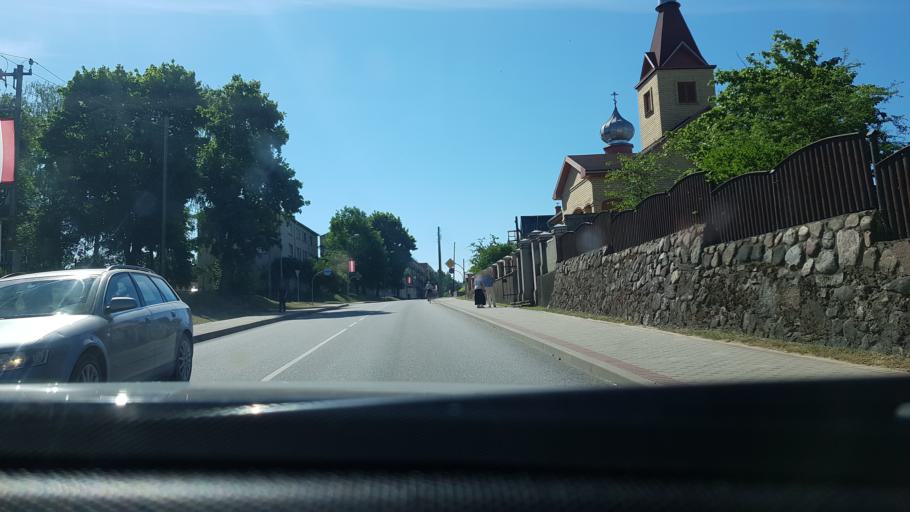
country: LV
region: Kraslavas Rajons
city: Kraslava
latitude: 55.8904
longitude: 27.1710
